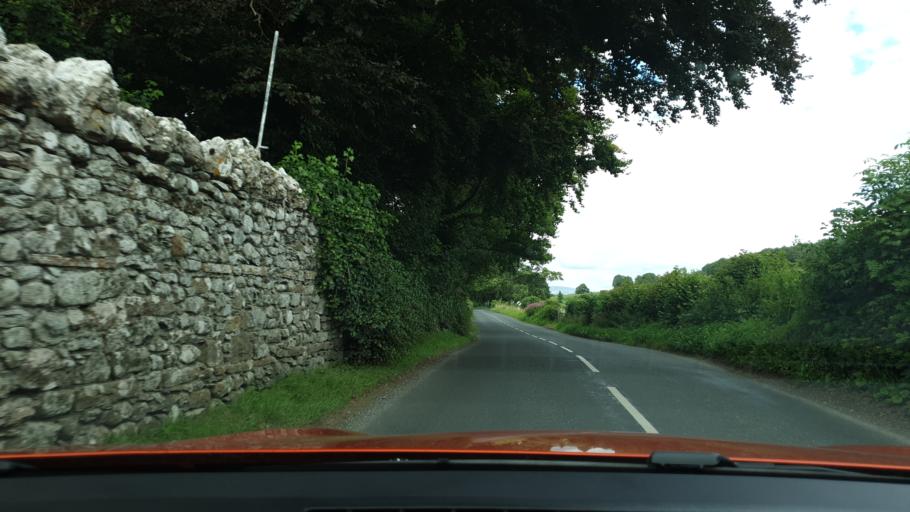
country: GB
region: England
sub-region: Cumbria
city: Penrith
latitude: 54.6175
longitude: -2.8091
